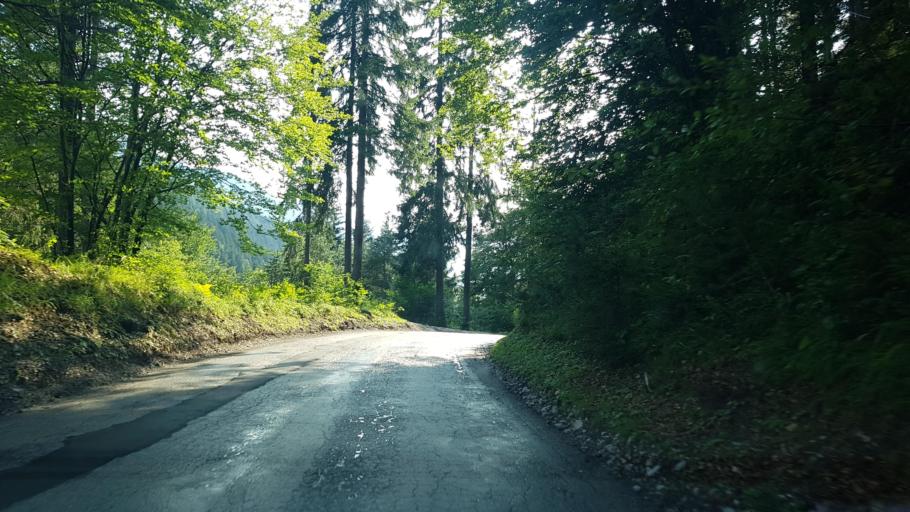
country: IT
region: Veneto
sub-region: Provincia di Belluno
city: San Pietro di Cadore
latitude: 46.5830
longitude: 12.6254
